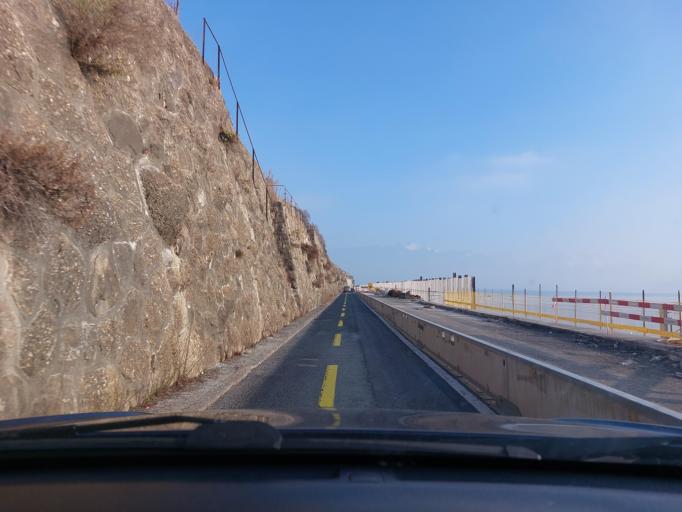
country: CH
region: Vaud
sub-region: Lavaux-Oron District
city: Chexbres
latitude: 46.4768
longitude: 6.7710
